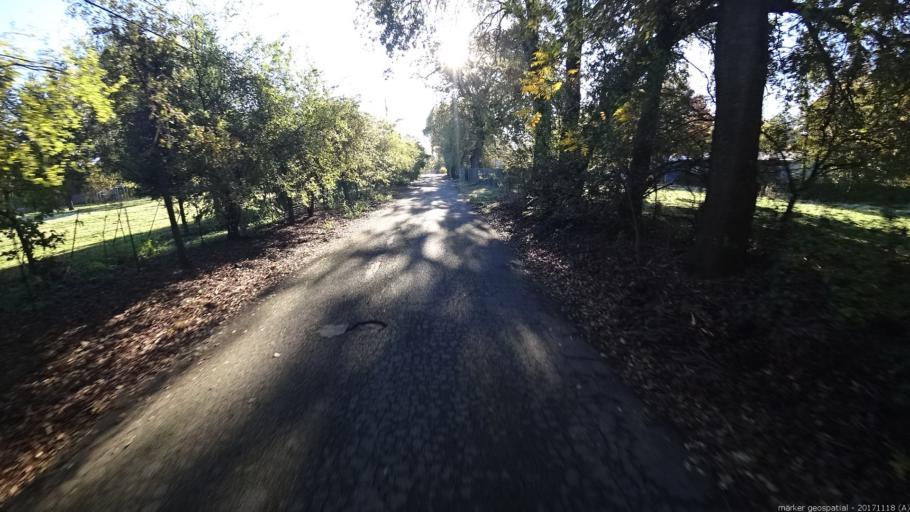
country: US
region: California
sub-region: Shasta County
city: Anderson
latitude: 40.4485
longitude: -122.2782
